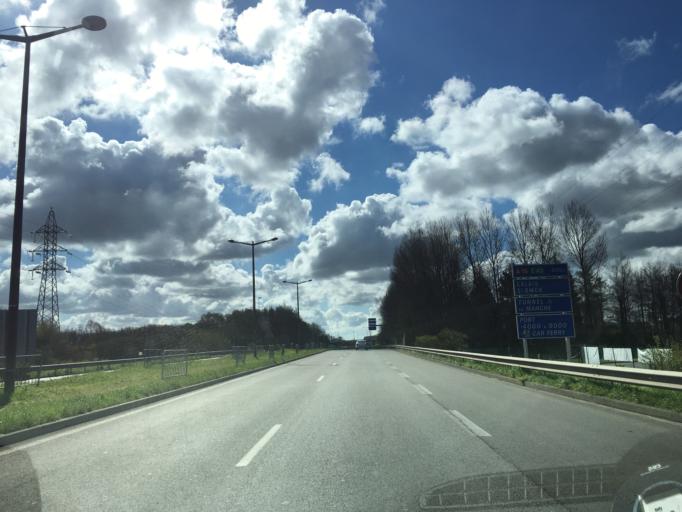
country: FR
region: Nord-Pas-de-Calais
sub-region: Departement du Nord
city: Grande-Synthe
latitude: 51.0044
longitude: 2.2868
